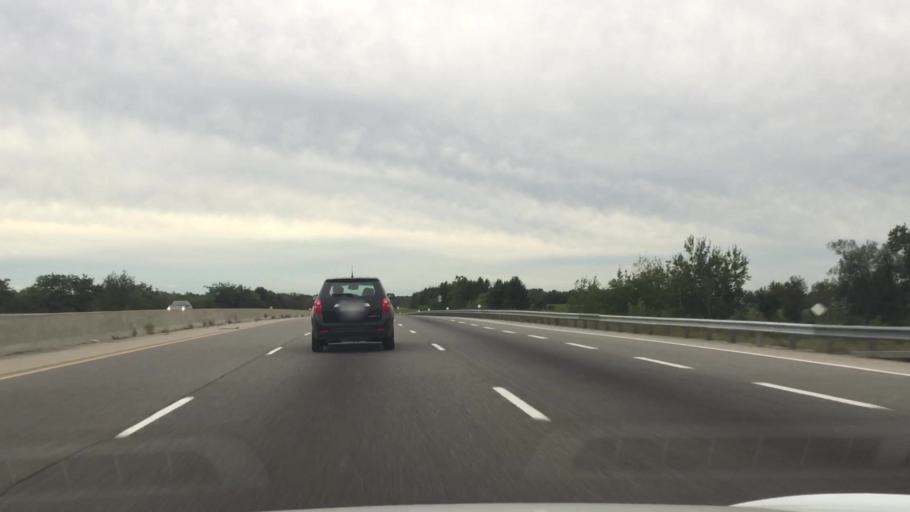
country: CA
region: Ontario
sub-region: Oxford County
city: Woodstock
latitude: 43.2229
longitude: -80.6031
